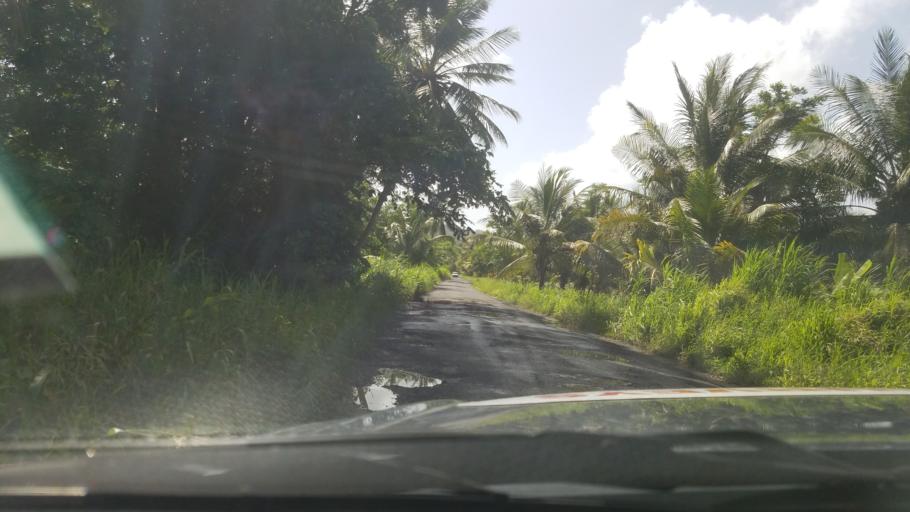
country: LC
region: Anse-la-Raye
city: Anse La Raye
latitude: 13.9558
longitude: -61.0106
